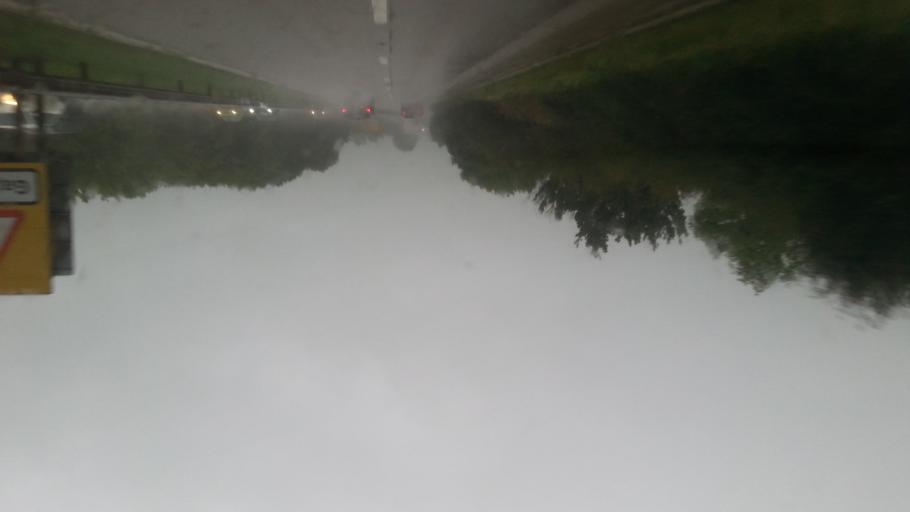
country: GB
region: England
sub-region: Leicestershire
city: Grimston
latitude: 52.8344
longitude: -1.0361
